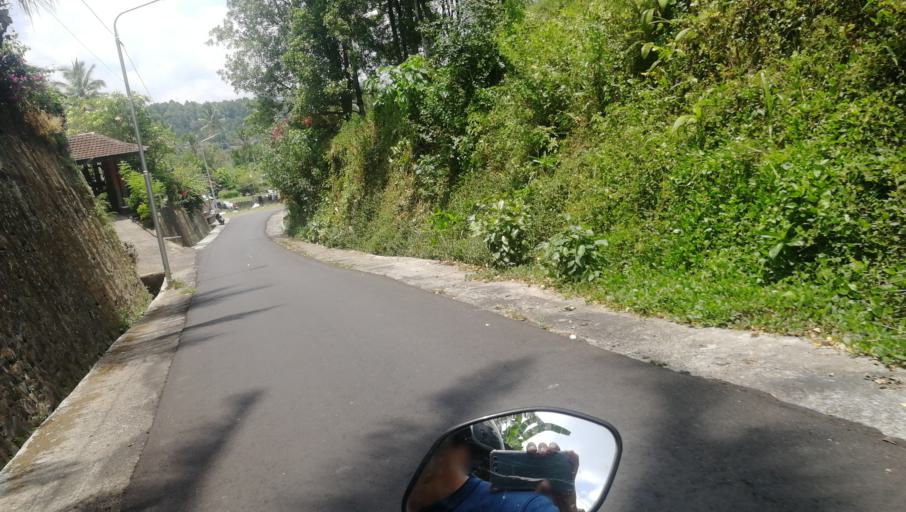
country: ID
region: Bali
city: Banjar Pedawa
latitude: -8.2629
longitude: 115.0308
